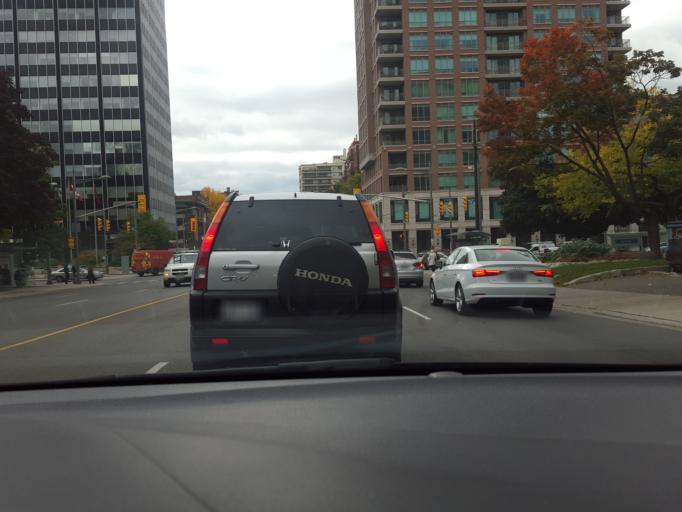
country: CA
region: Ontario
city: Toronto
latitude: 43.6871
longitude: -79.4017
